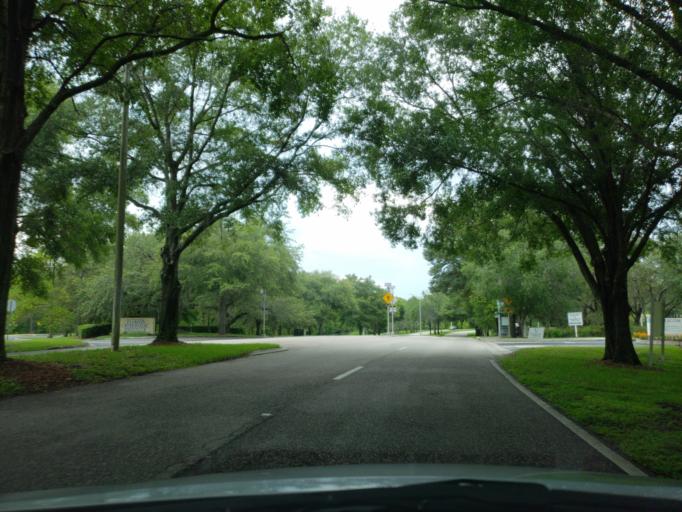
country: US
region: Florida
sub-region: Hillsborough County
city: Temple Terrace
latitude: 28.0637
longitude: -82.3719
